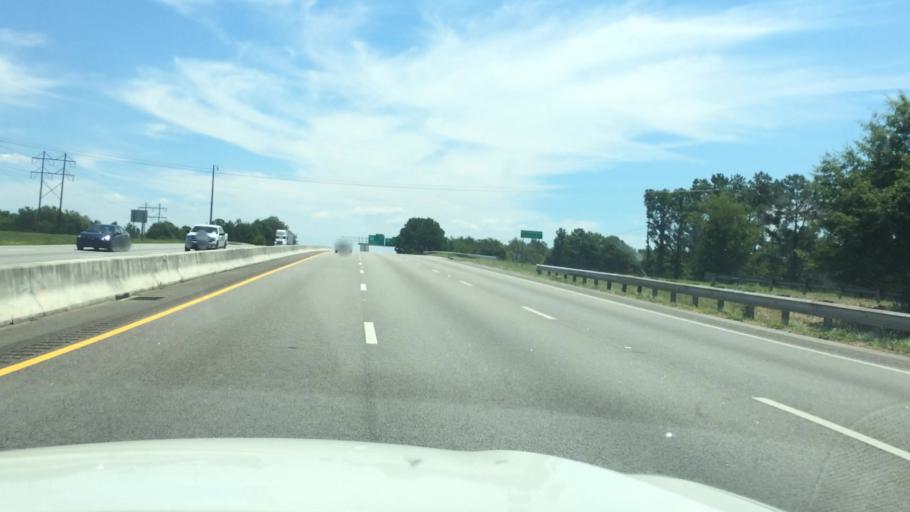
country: US
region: South Carolina
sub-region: Richland County
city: Dentsville
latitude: 34.0730
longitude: -80.9807
